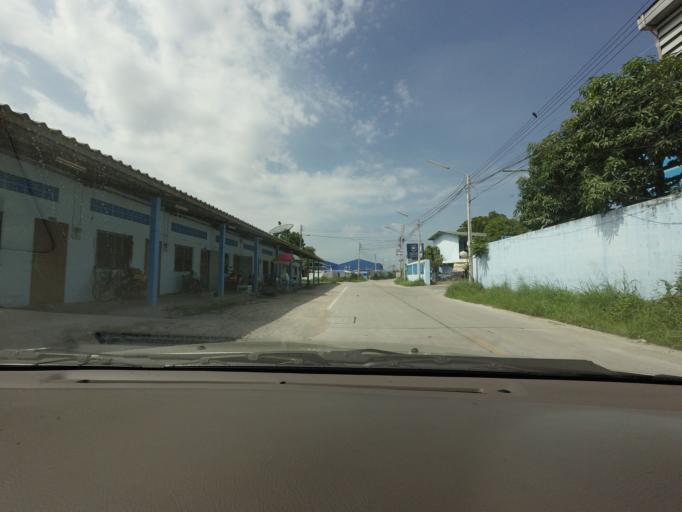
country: TH
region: Chon Buri
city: Chon Buri
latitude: 13.3270
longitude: 101.0043
